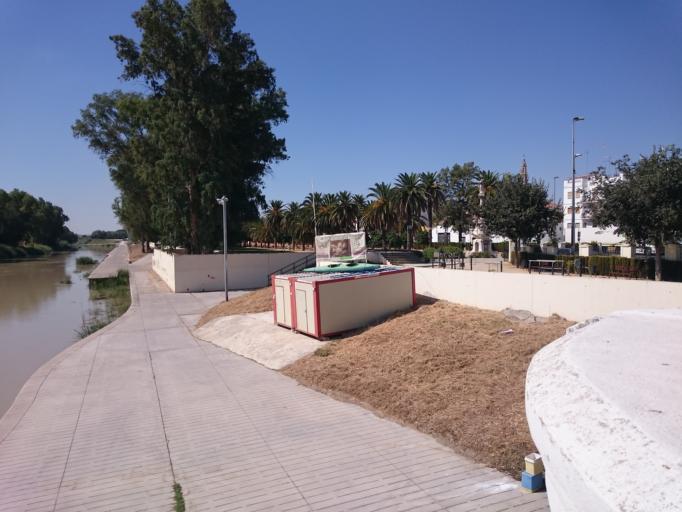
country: ES
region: Andalusia
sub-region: Provincia de Sevilla
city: Ecija
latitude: 37.5436
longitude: -5.0724
